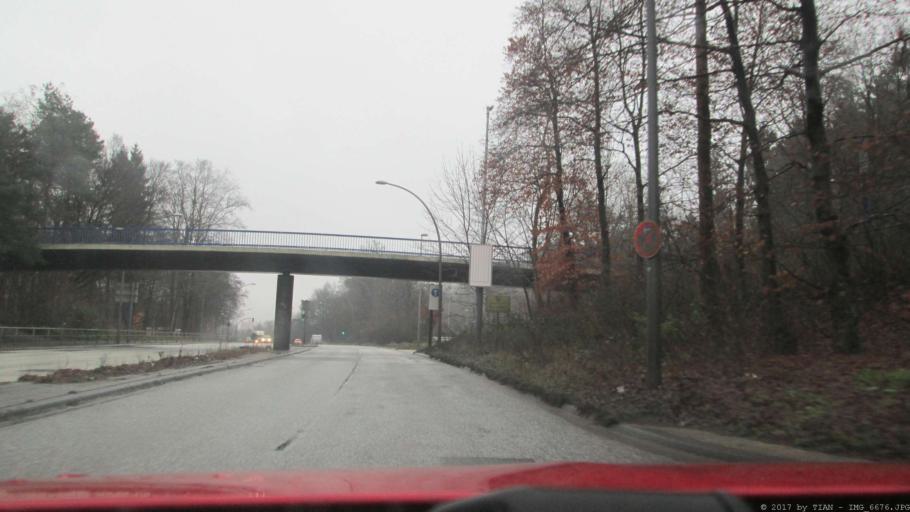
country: DE
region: Hamburg
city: Eidelstedt
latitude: 53.5867
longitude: 9.9051
